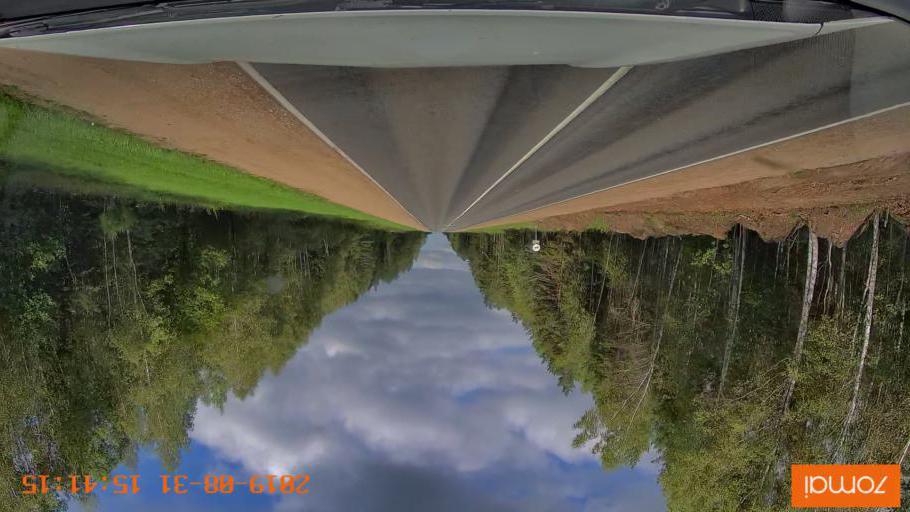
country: RU
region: Kaluga
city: Mosal'sk
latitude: 54.6379
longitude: 34.8558
